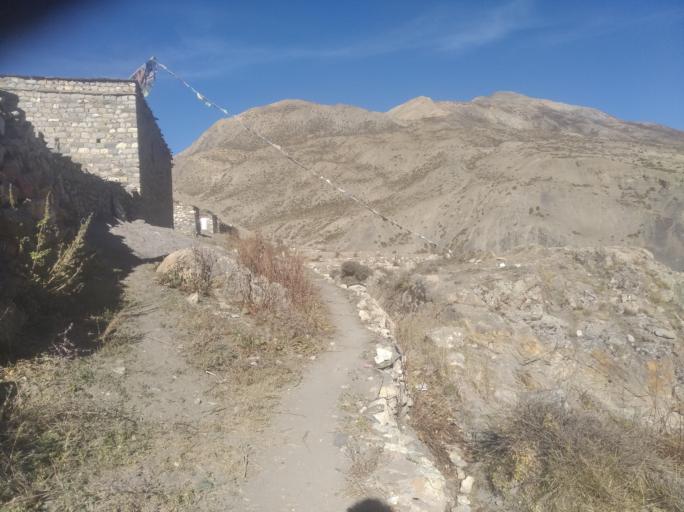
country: NP
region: Western Region
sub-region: Dhawalagiri Zone
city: Jomsom
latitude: 29.0913
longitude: 83.4139
